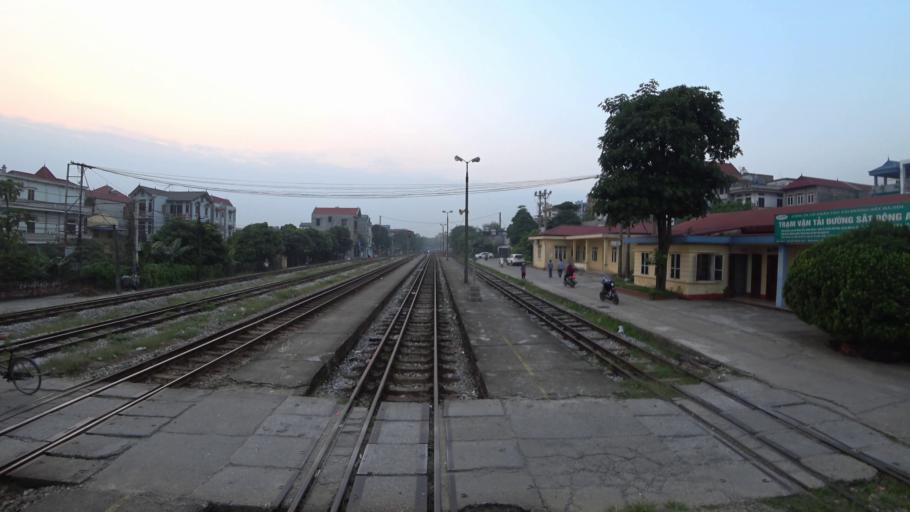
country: VN
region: Ha Noi
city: Dong Anh
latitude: 21.1583
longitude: 105.8471
